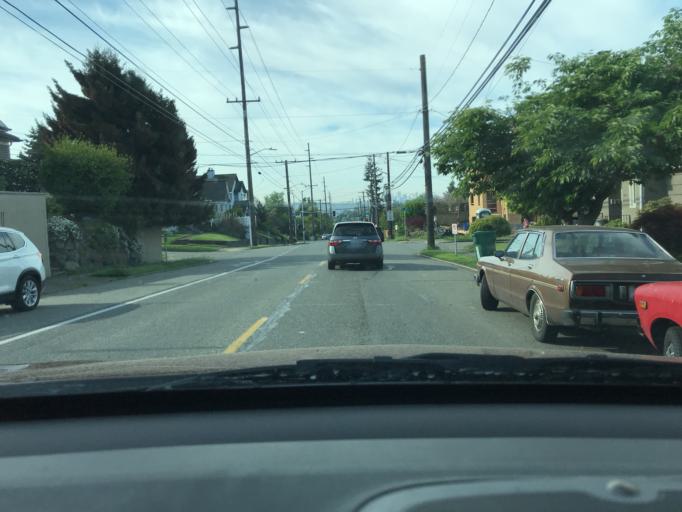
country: US
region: Washington
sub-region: King County
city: Shoreline
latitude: 47.6880
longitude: -122.3230
